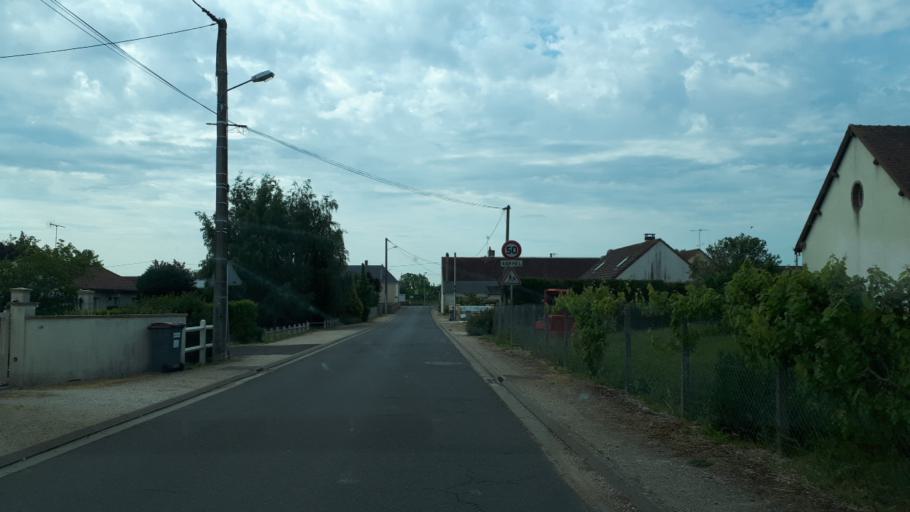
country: FR
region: Centre
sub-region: Departement du Loir-et-Cher
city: Villiers-sur-Loir
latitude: 47.7492
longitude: 0.9883
